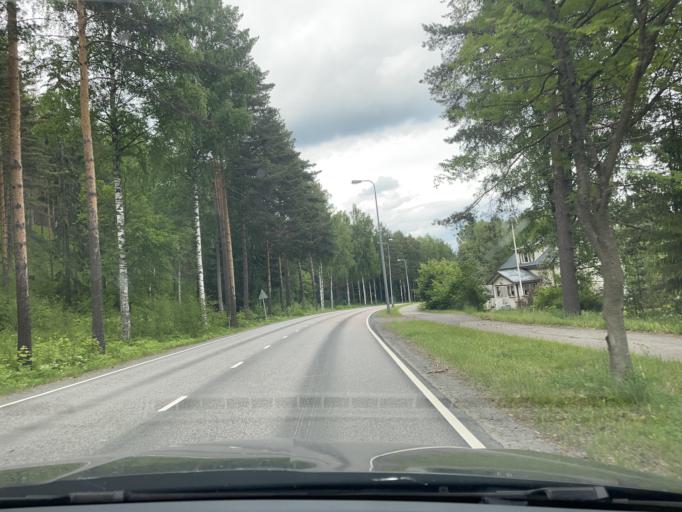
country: FI
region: Central Finland
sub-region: Jaemsae
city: Jaemsaenkoski
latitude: 61.9205
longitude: 25.1514
